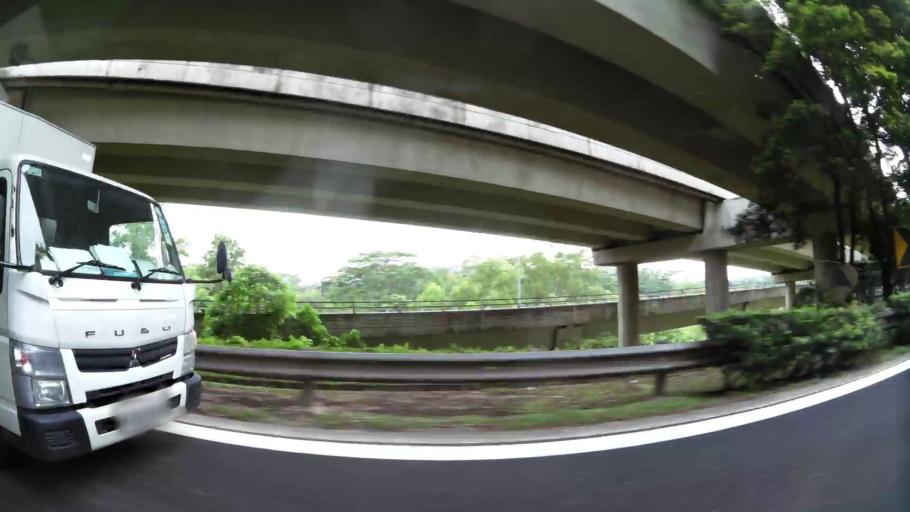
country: MY
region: Johor
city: Johor Bahru
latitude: 1.4193
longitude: 103.7702
